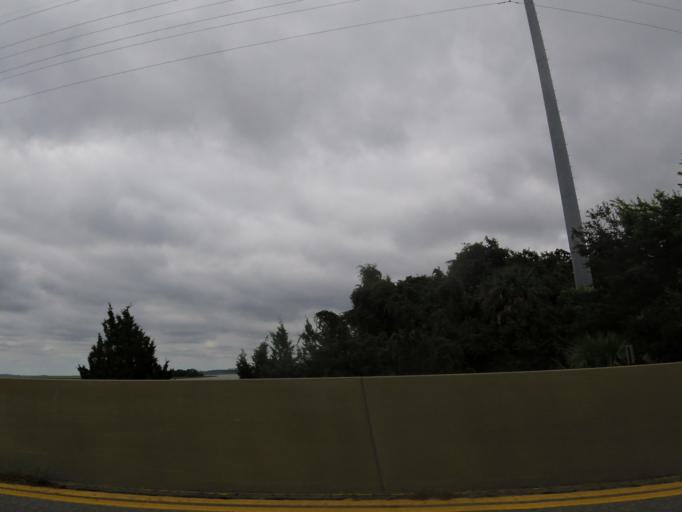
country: US
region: Georgia
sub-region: Glynn County
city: Saint Simon Mills
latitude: 31.1668
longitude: -81.4119
